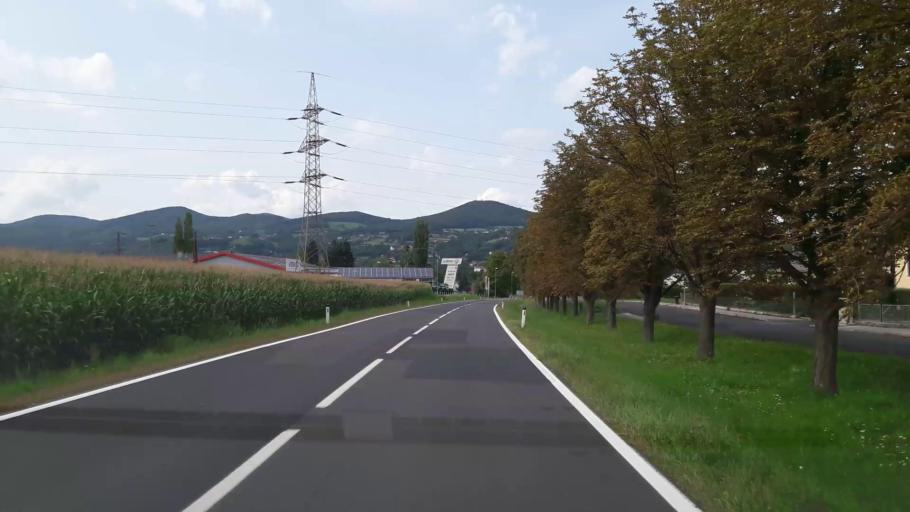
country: AT
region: Styria
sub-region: Politischer Bezirk Hartberg-Fuerstenfeld
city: Hartberg
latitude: 47.2626
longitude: 15.9705
